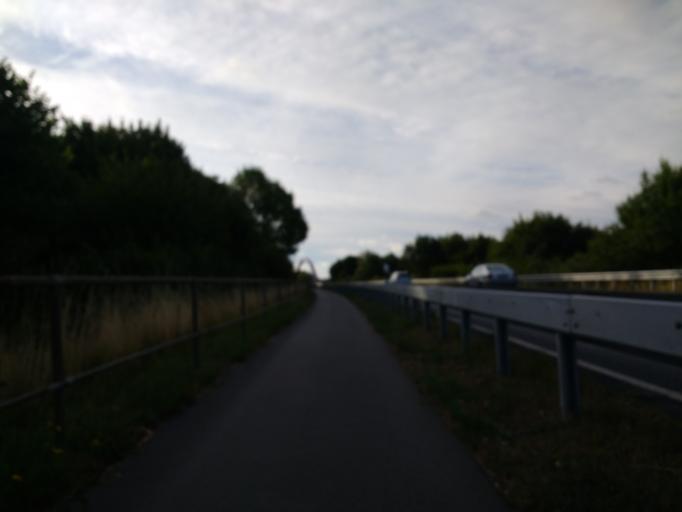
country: DE
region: Lower Saxony
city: Wasbuttel
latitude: 52.4286
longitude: 10.6025
